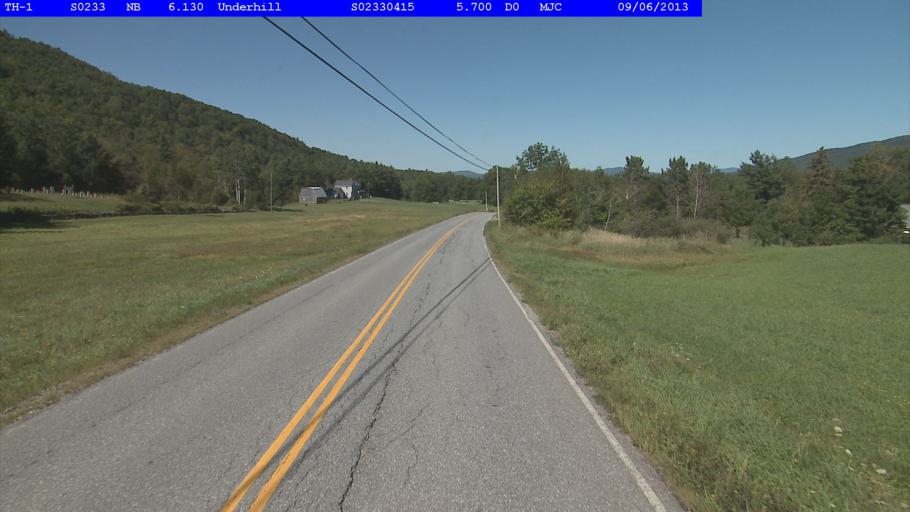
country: US
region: Vermont
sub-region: Chittenden County
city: Jericho
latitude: 44.5471
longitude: -72.8680
